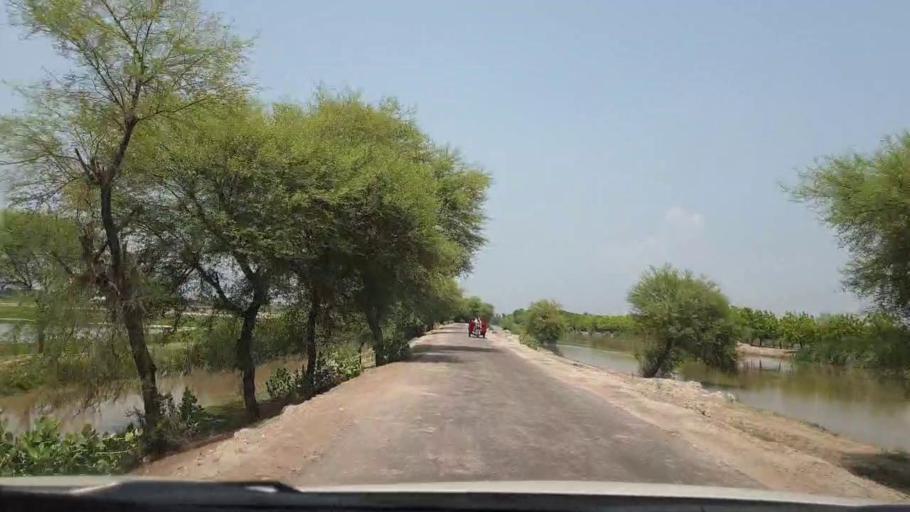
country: PK
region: Sindh
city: Dokri
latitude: 27.3556
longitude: 68.1131
